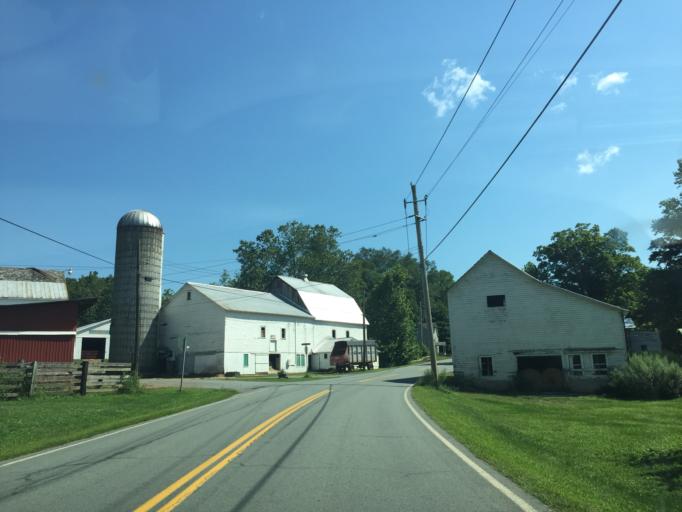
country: US
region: New York
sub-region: Sullivan County
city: Livingston Manor
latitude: 41.7939
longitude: -75.0131
